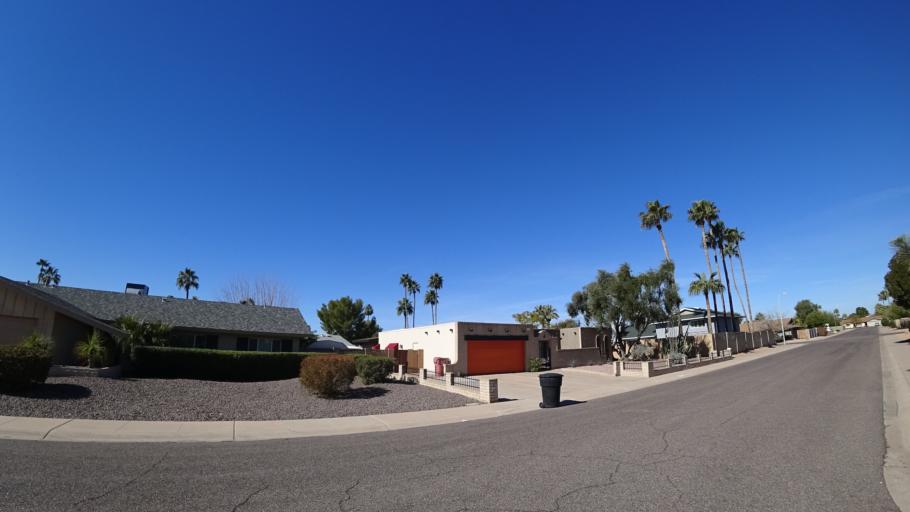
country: US
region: Arizona
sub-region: Maricopa County
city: Scottsdale
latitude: 33.5174
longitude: -111.9024
